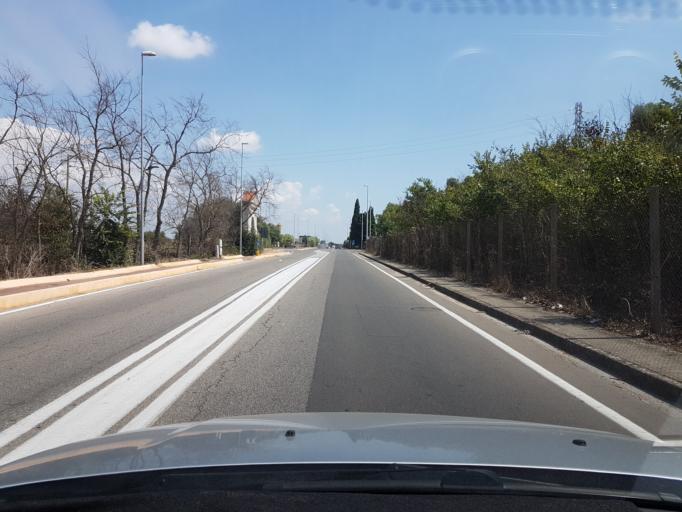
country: IT
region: Sardinia
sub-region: Provincia di Oristano
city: Sili
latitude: 39.9121
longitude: 8.6077
